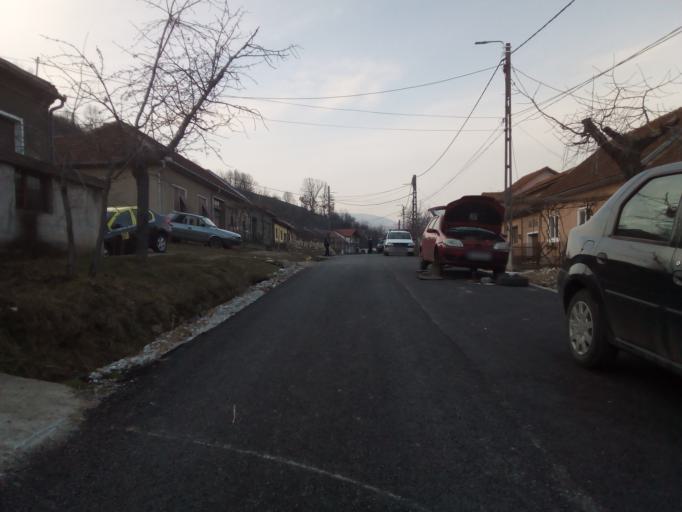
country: RO
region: Mehedinti
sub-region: Comuna Eselnita
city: Eselnita
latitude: 44.6919
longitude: 22.3637
